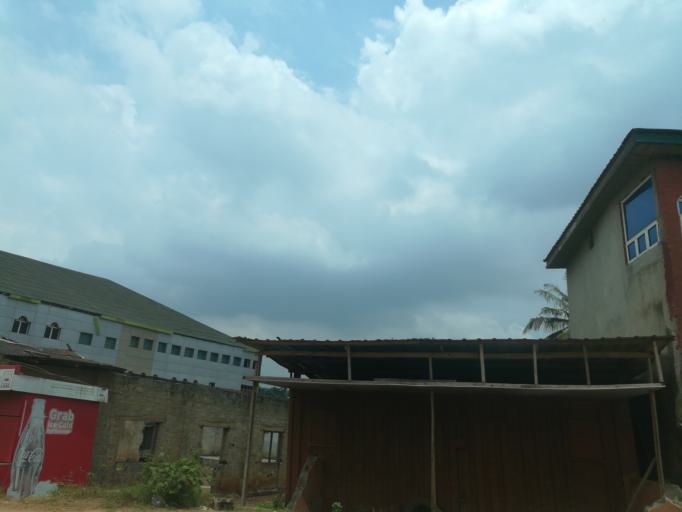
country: NG
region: Lagos
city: Ikorodu
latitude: 6.6255
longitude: 3.5270
